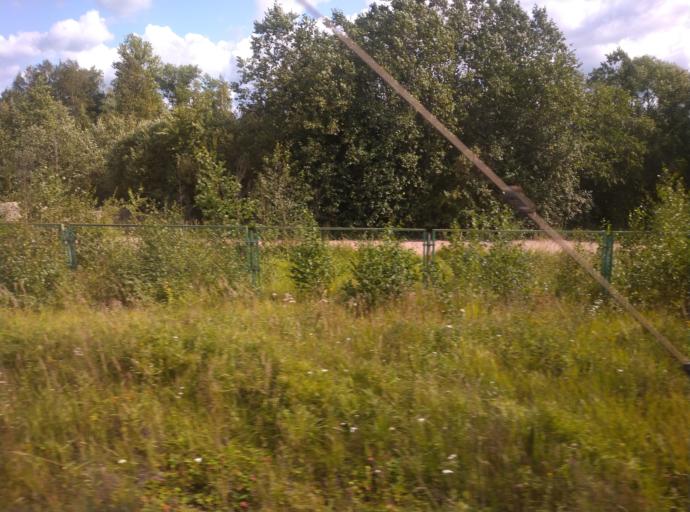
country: RU
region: Leningrad
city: Krasnyy Bor
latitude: 59.6797
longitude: 30.7022
